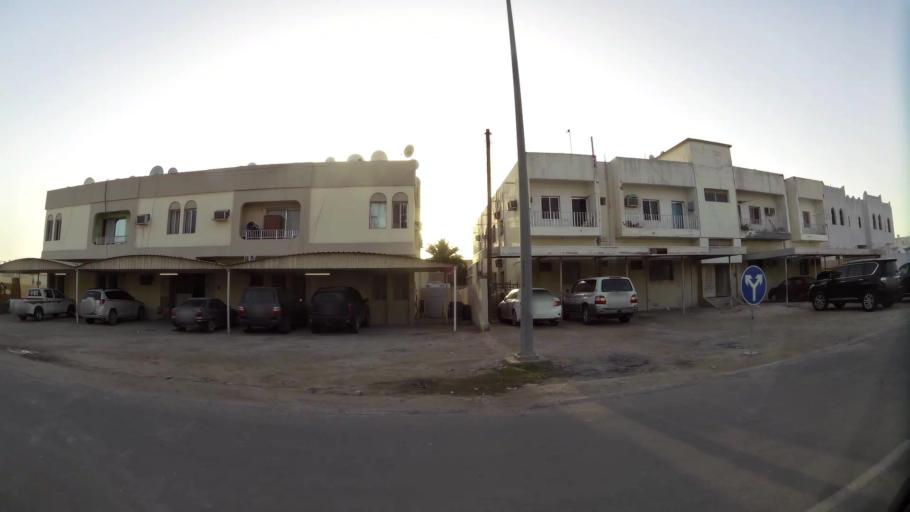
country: QA
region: Baladiyat ar Rayyan
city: Ar Rayyan
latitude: 25.3181
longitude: 51.4582
